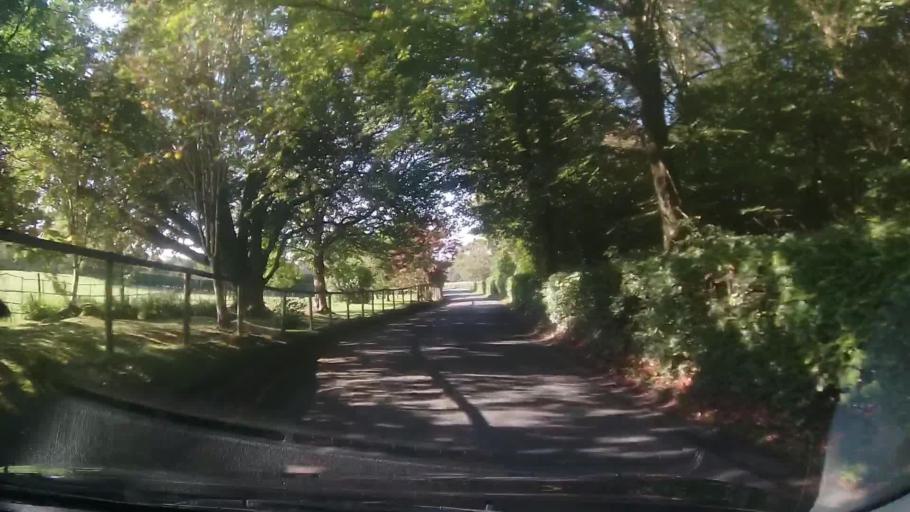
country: GB
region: England
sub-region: Cumbria
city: Seascale
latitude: 54.3988
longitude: -3.3775
